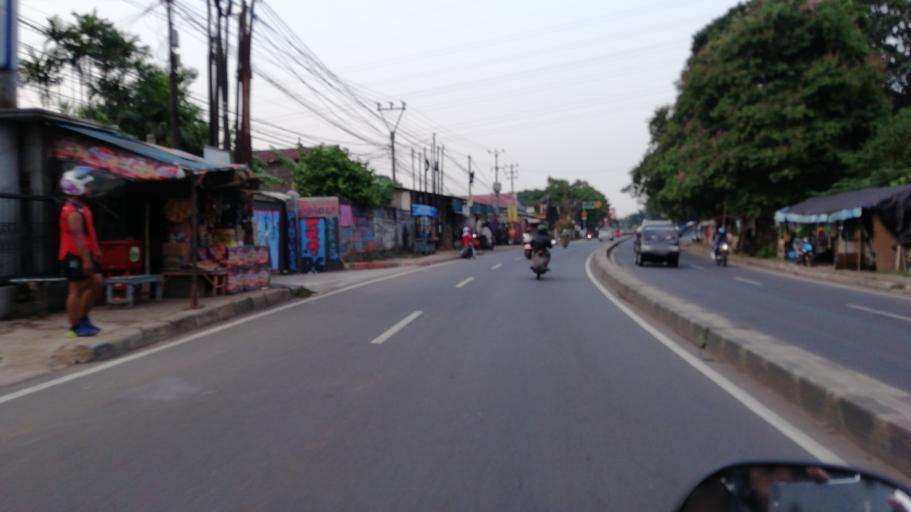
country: ID
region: West Java
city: Depok
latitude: -6.4219
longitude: 106.8570
